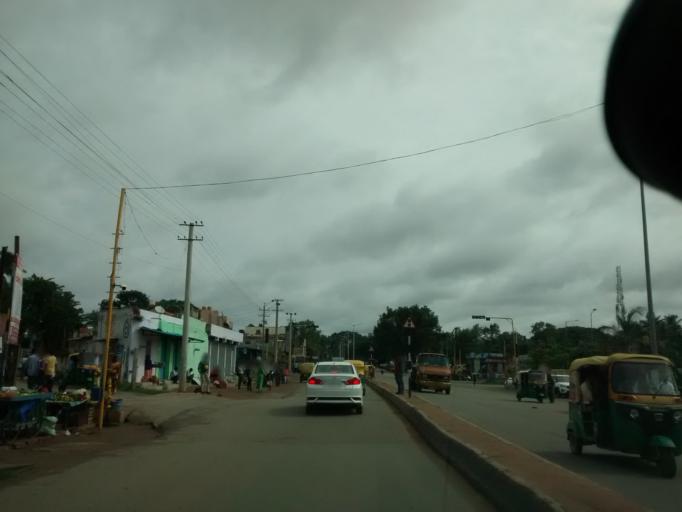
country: IN
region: Karnataka
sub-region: Tumkur
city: Tumkur
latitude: 13.3624
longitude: 77.1033
